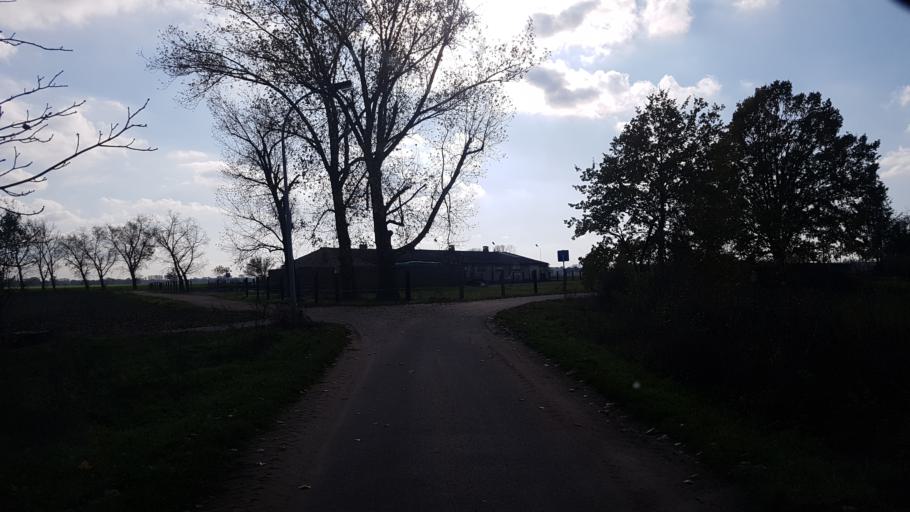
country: DE
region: Brandenburg
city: Schonewalde
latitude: 51.6936
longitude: 13.5718
